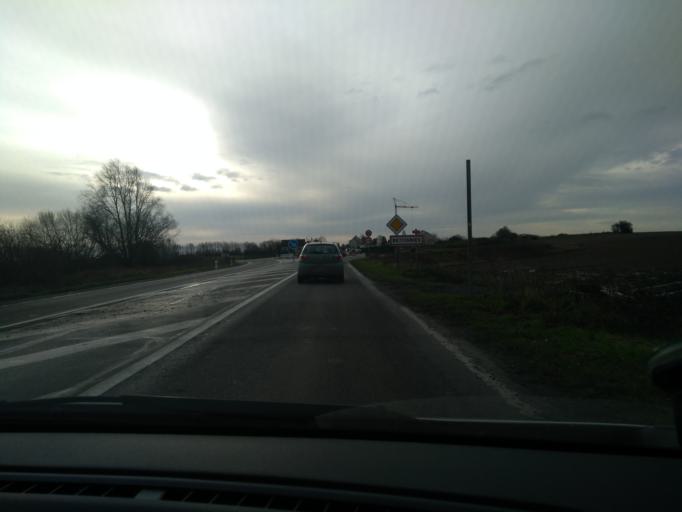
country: BE
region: Wallonia
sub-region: Province du Hainaut
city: Quevy-le-Petit
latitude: 50.3432
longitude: 3.9706
